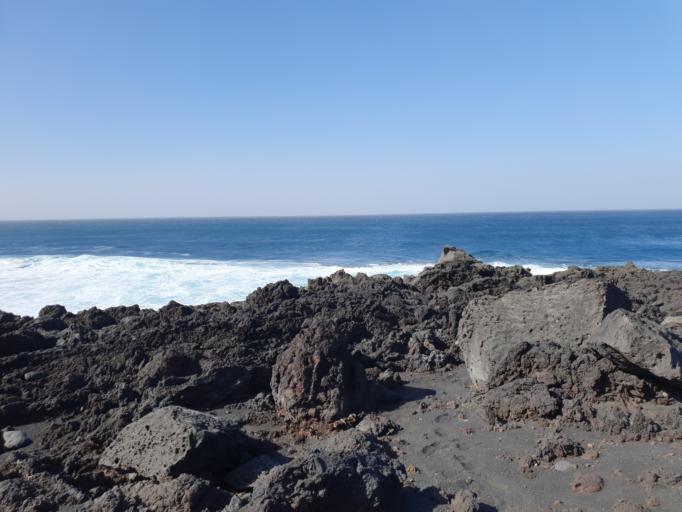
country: ES
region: Canary Islands
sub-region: Provincia de Las Palmas
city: Tinajo
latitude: 29.0665
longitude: -13.7620
